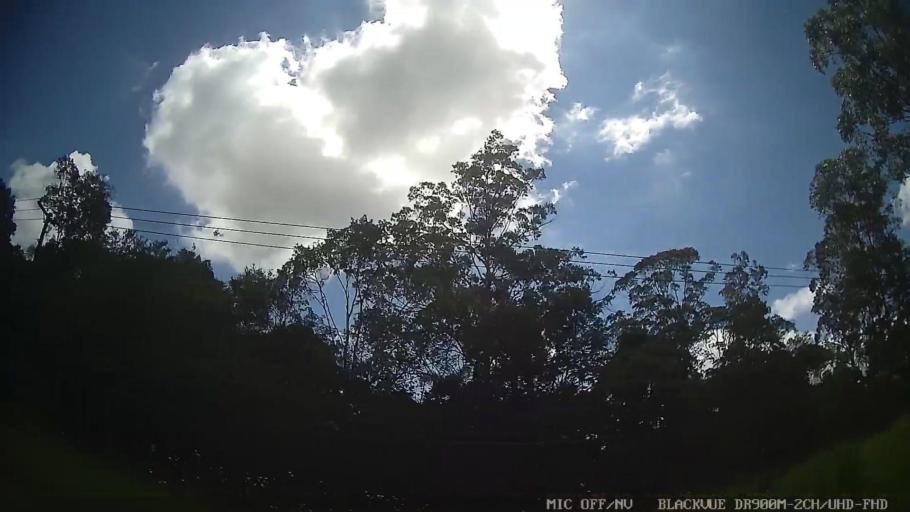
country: BR
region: Sao Paulo
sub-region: Mogi das Cruzes
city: Mogi das Cruzes
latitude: -23.6709
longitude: -46.2091
